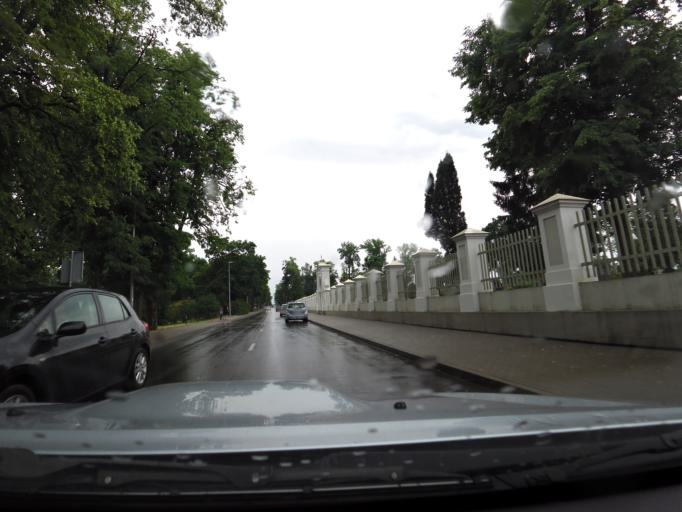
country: LT
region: Marijampoles apskritis
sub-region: Marijampole Municipality
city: Marijampole
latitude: 54.5498
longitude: 23.3461
